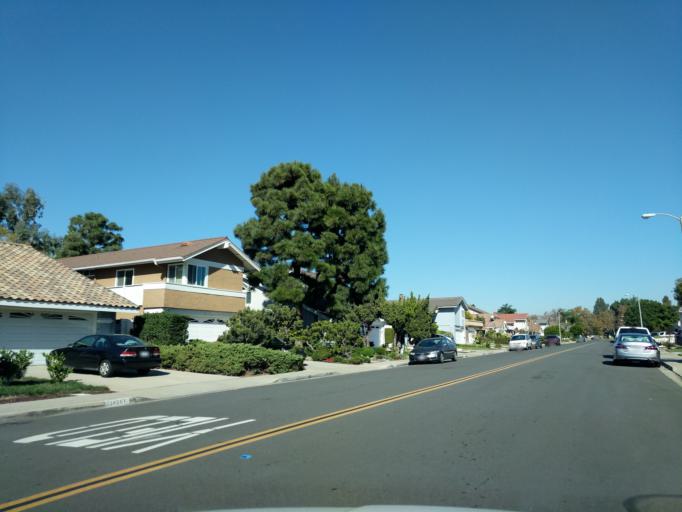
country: US
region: California
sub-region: Orange County
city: Irvine
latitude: 33.7083
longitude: -117.7872
